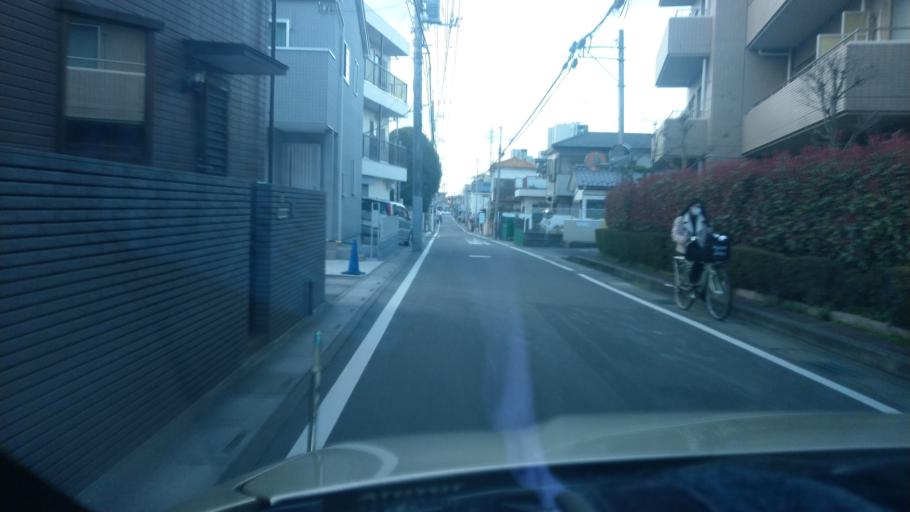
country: JP
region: Saitama
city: Yono
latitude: 35.8971
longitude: 139.5998
